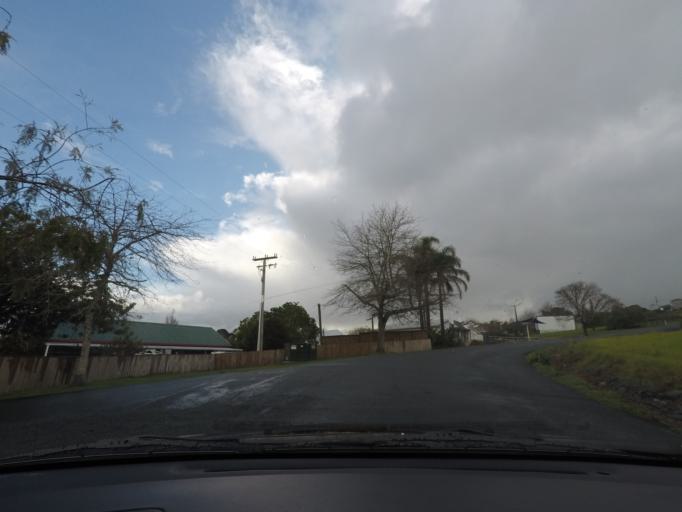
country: NZ
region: Auckland
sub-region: Auckland
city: Warkworth
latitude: -36.4295
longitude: 174.7313
